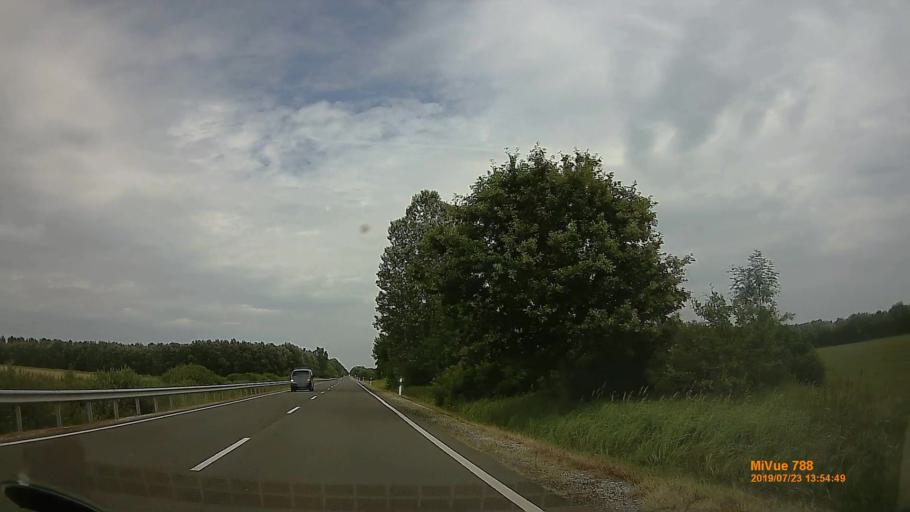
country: HU
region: Hajdu-Bihar
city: Gorbehaza
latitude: 47.9172
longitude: 21.2029
